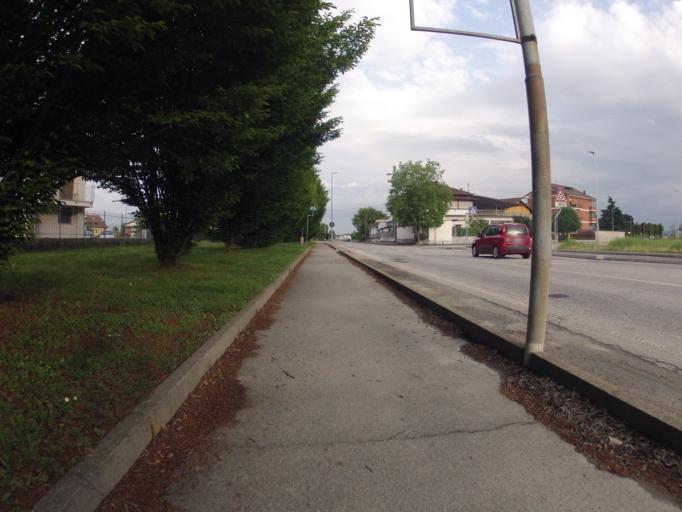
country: IT
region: Piedmont
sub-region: Provincia di Cuneo
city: Moretta
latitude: 44.7599
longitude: 7.5342
